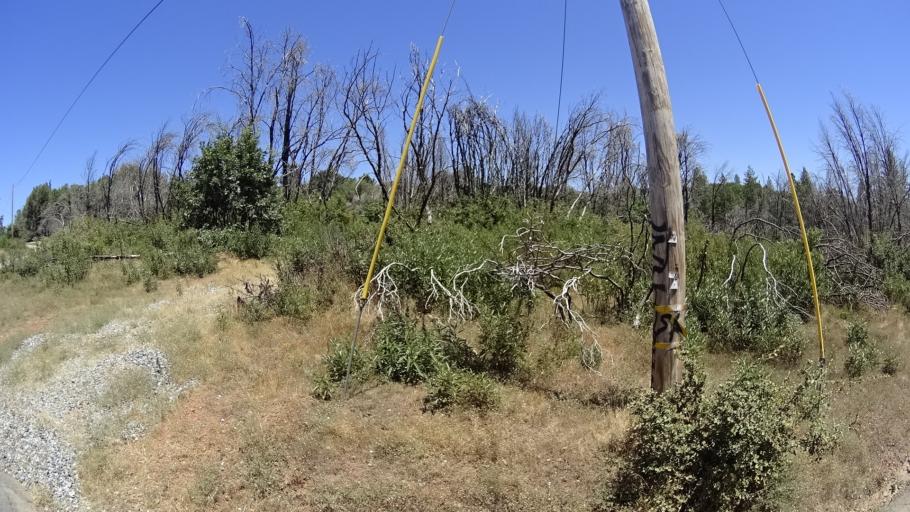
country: US
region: California
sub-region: Calaveras County
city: Mountain Ranch
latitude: 38.2370
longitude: -120.6126
